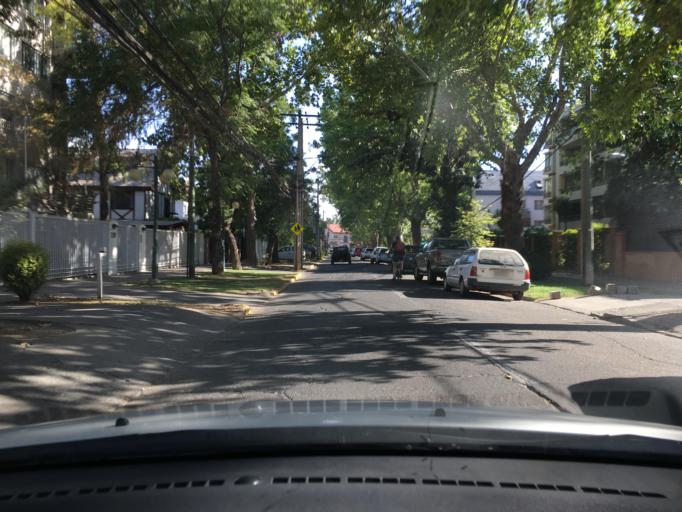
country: CL
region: Santiago Metropolitan
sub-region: Provincia de Santiago
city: Villa Presidente Frei, Nunoa, Santiago, Chile
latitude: -33.4578
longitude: -70.5922
